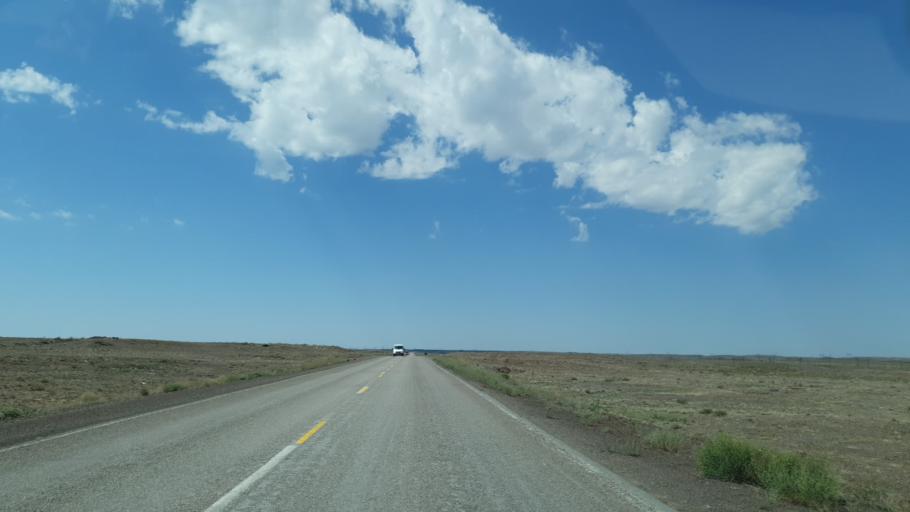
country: KZ
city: Priozersk
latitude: 45.8801
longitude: 73.4869
